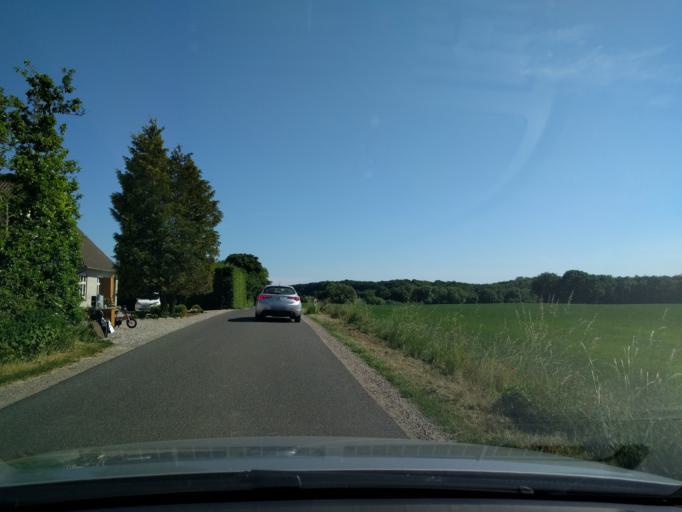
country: DK
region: South Denmark
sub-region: Nyborg Kommune
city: Ullerslev
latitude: 55.3833
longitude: 10.6407
